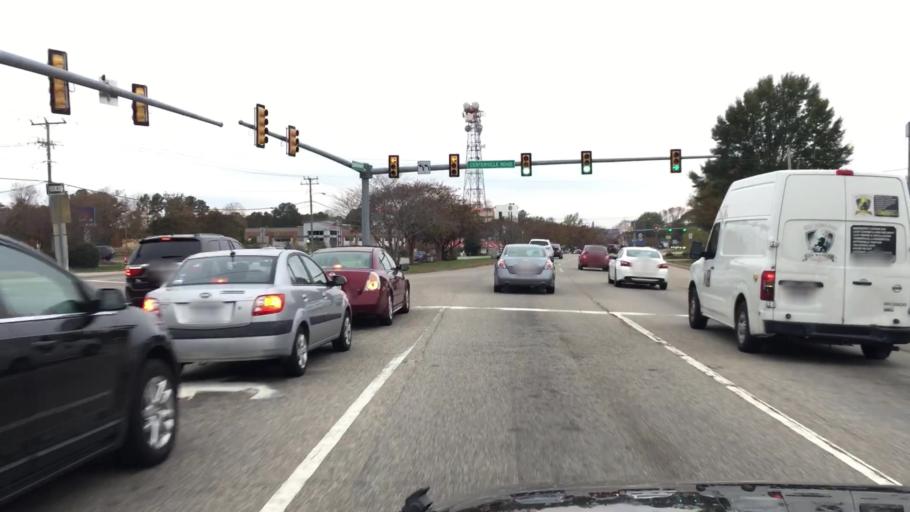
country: US
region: Virginia
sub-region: James City County
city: Williamsburg
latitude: 37.3385
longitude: -76.7528
